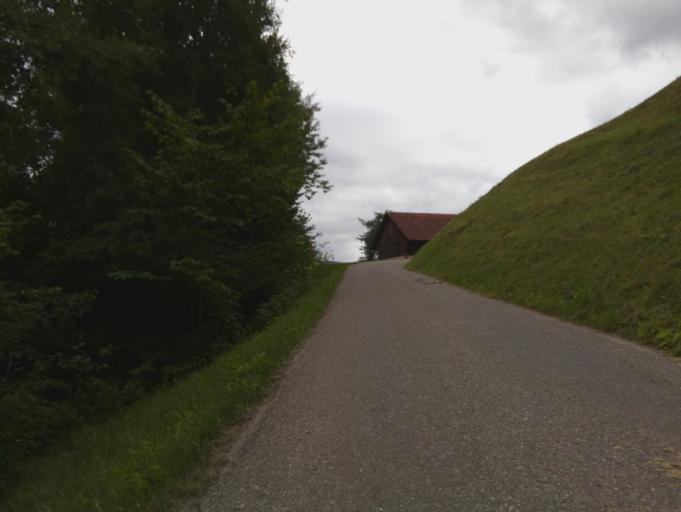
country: CH
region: Saint Gallen
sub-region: Wahlkreis Toggenburg
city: Buetschwil
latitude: 47.3555
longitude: 9.0784
